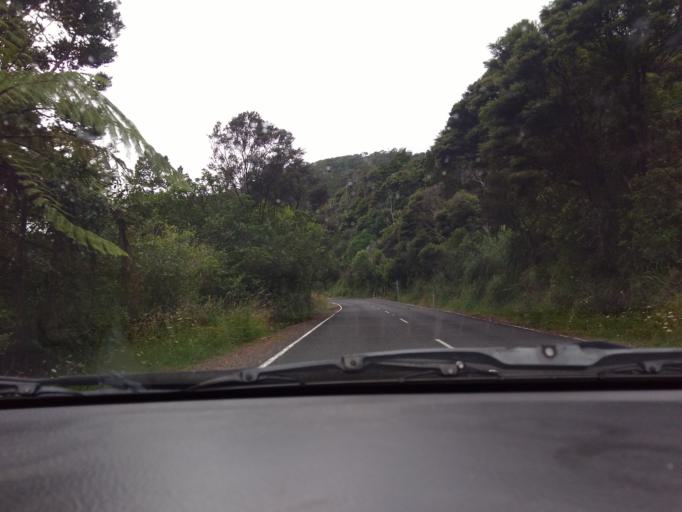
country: NZ
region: Auckland
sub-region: Auckland
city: Titirangi
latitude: -37.0058
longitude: 174.5786
